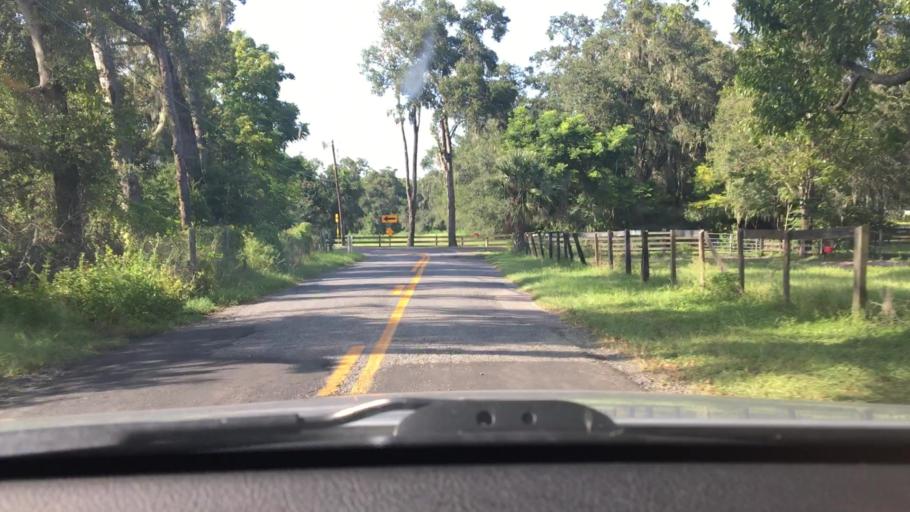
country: US
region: Florida
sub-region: Volusia County
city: Lake Helen
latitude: 28.9699
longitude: -81.2151
